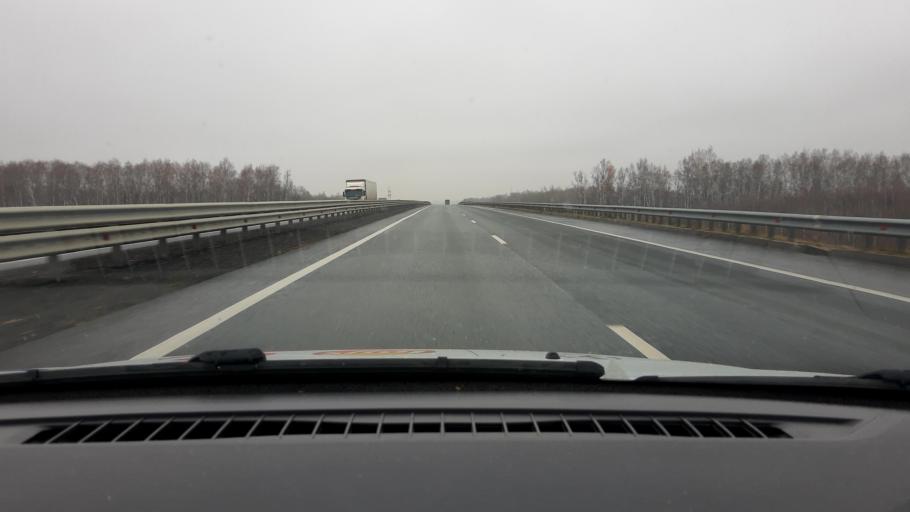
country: RU
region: Nizjnij Novgorod
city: Burevestnik
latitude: 56.1307
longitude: 43.7796
